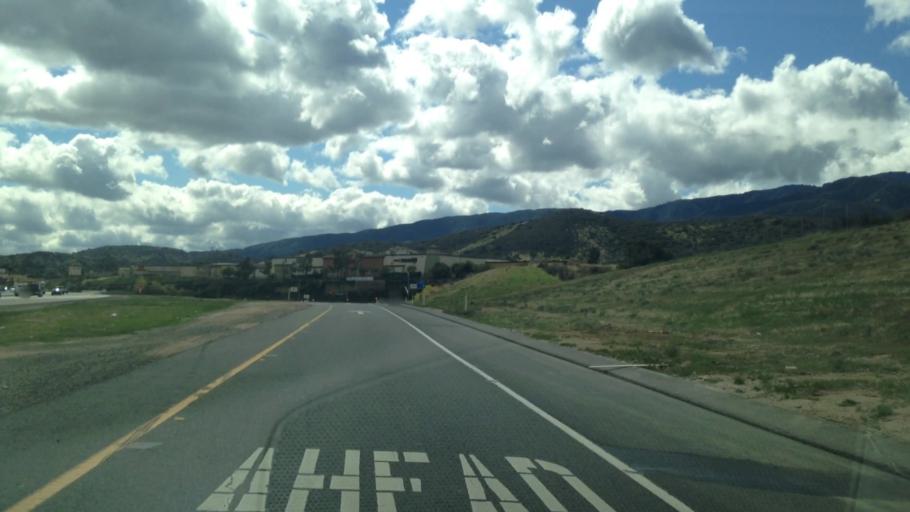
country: US
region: California
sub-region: Riverside County
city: El Cerrito
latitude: 33.7508
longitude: -117.4551
